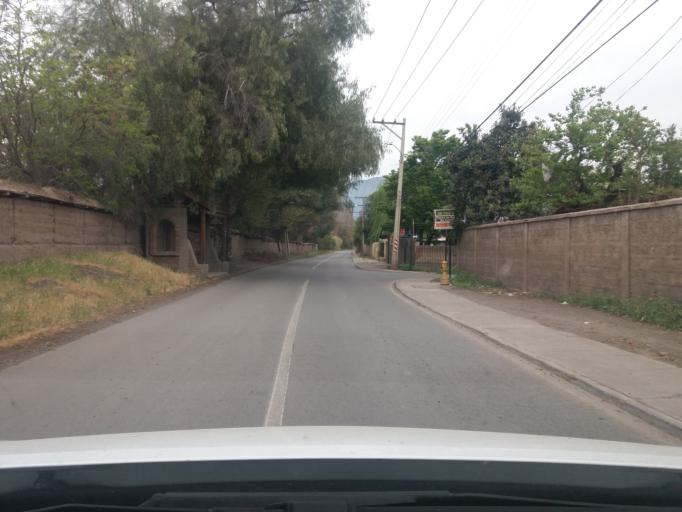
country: CL
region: Valparaiso
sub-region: Provincia de Los Andes
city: Los Andes
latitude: -32.8450
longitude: -70.6292
